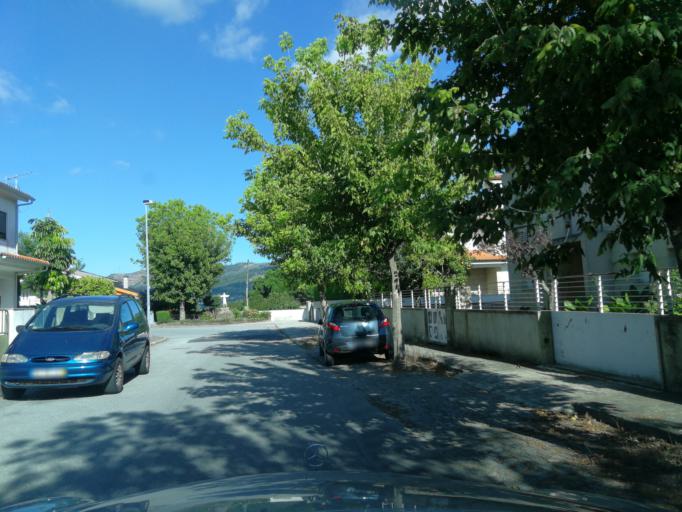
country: PT
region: Braga
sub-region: Braga
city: Adaufe
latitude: 41.5700
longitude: -8.3857
